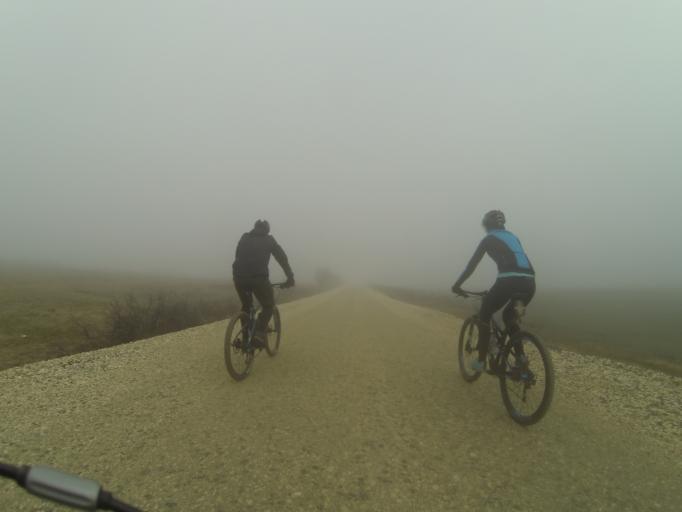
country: RO
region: Mehedinti
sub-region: Comuna Balacita
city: Gvardinita
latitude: 44.4346
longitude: 23.1342
